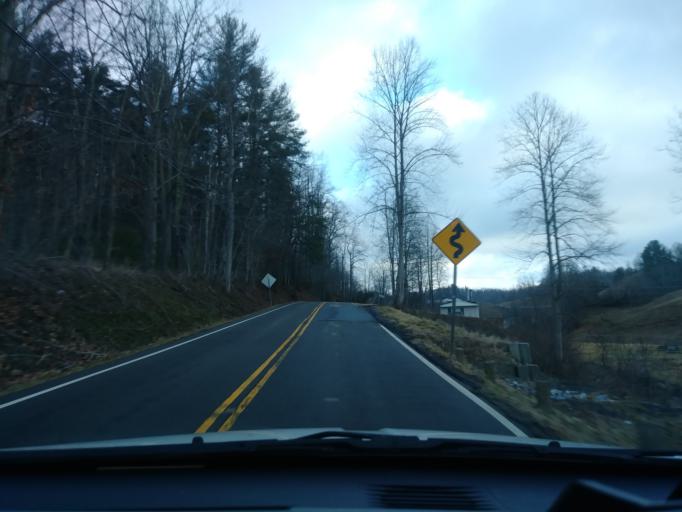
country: US
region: Tennessee
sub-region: Unicoi County
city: Unicoi
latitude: 36.1916
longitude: -82.2479
